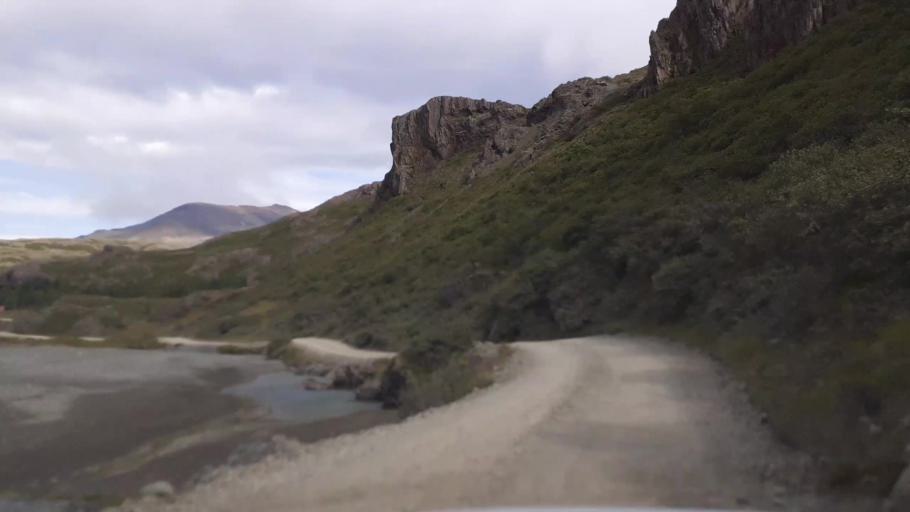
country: IS
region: East
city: Hoefn
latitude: 64.4317
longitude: -14.8910
